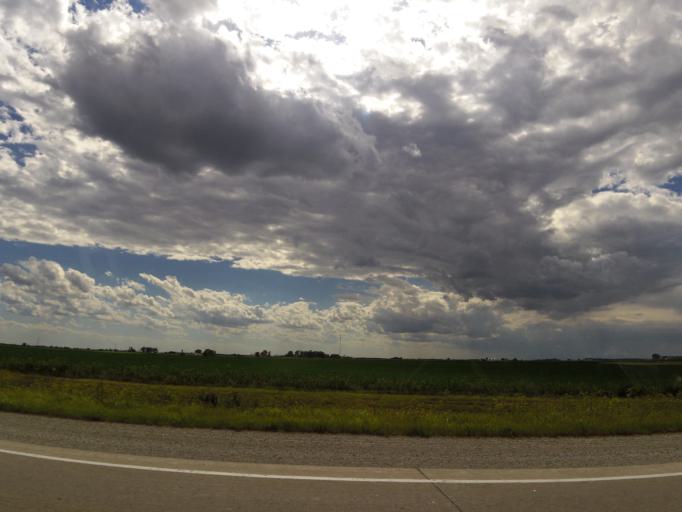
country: US
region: Iowa
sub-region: Henry County
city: Mount Pleasant
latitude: 40.8229
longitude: -91.5647
